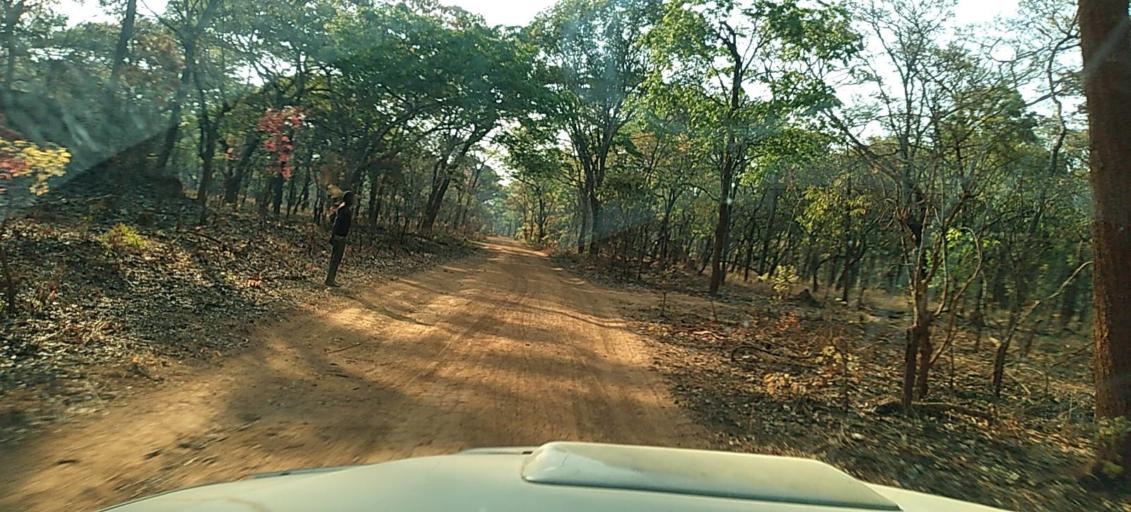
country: ZM
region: North-Western
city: Kasempa
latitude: -13.1676
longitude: 25.8924
